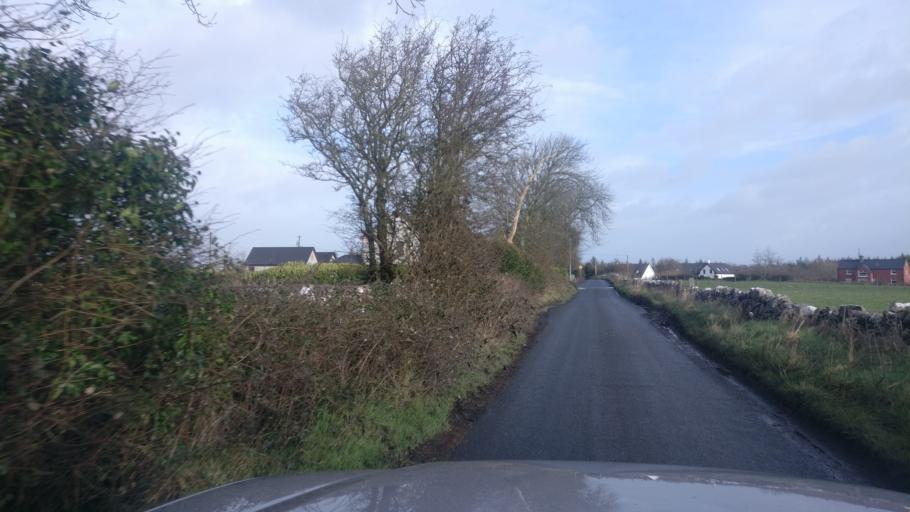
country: IE
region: Connaught
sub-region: County Galway
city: Loughrea
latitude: 53.2767
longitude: -8.5837
